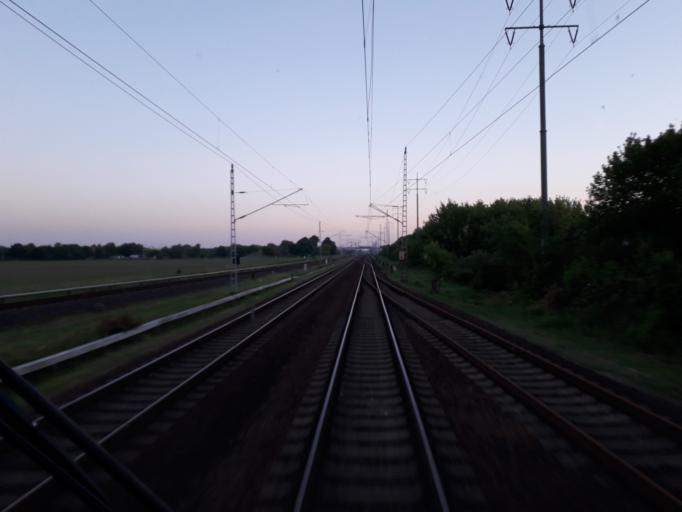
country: DE
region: Berlin
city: Blankenburg
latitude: 52.6130
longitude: 13.4516
